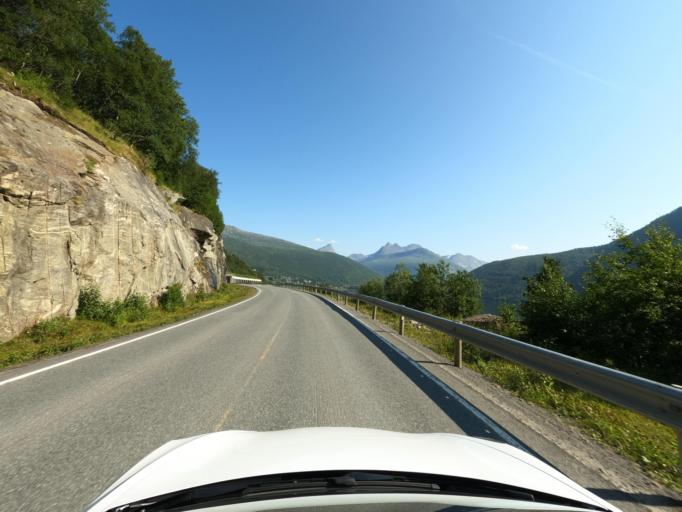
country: NO
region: Nordland
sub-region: Narvik
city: Narvik
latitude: 68.3869
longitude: 17.5575
